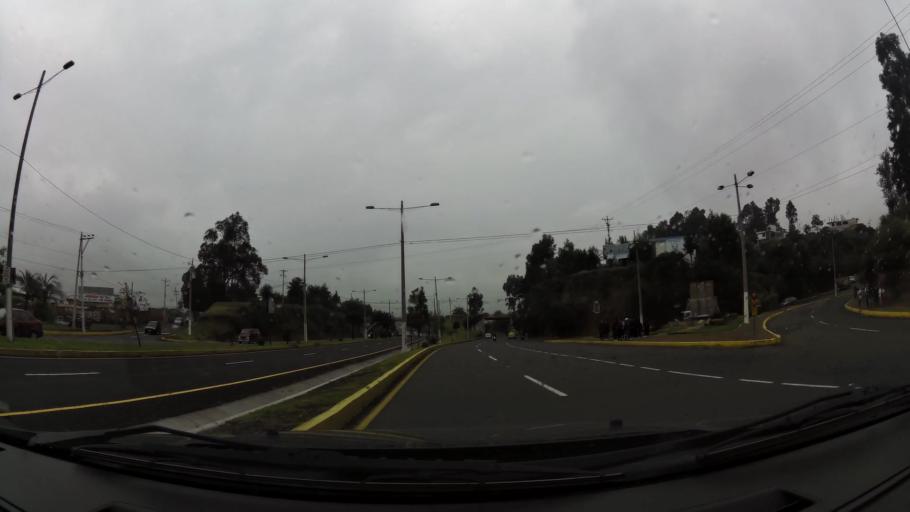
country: EC
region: Pichincha
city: Sangolqui
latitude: -0.2829
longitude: -78.4705
